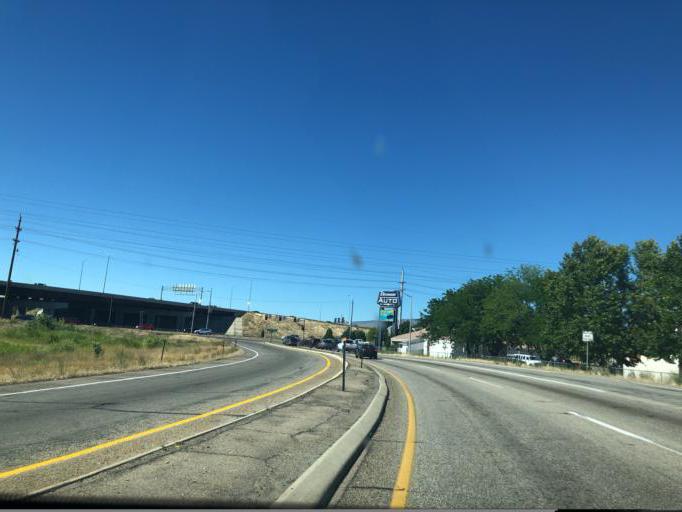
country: US
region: Idaho
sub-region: Ada County
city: Garden City
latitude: 43.6035
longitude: -116.2774
